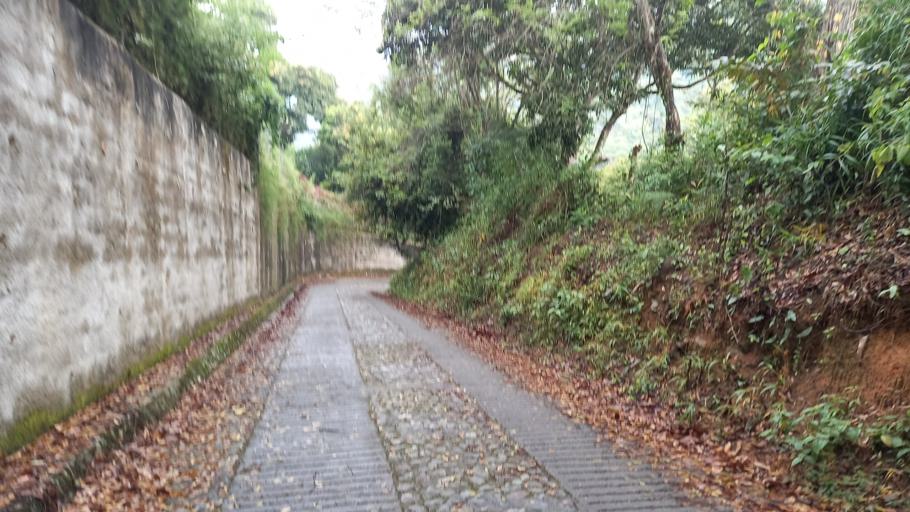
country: CO
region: Antioquia
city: Santa Barbara
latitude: 5.8483
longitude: -75.5751
